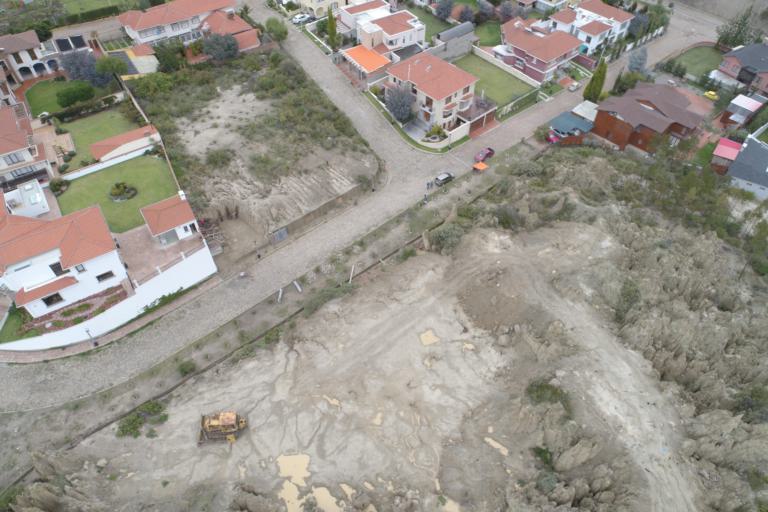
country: BO
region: La Paz
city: La Paz
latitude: -16.5577
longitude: -68.1106
